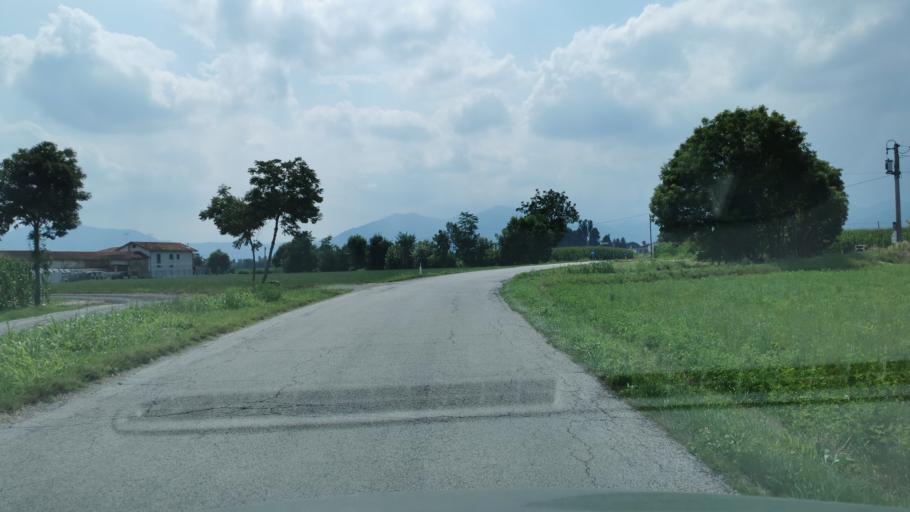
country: IT
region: Piedmont
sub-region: Provincia di Cuneo
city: Roata Rossi
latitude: 44.4314
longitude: 7.4892
